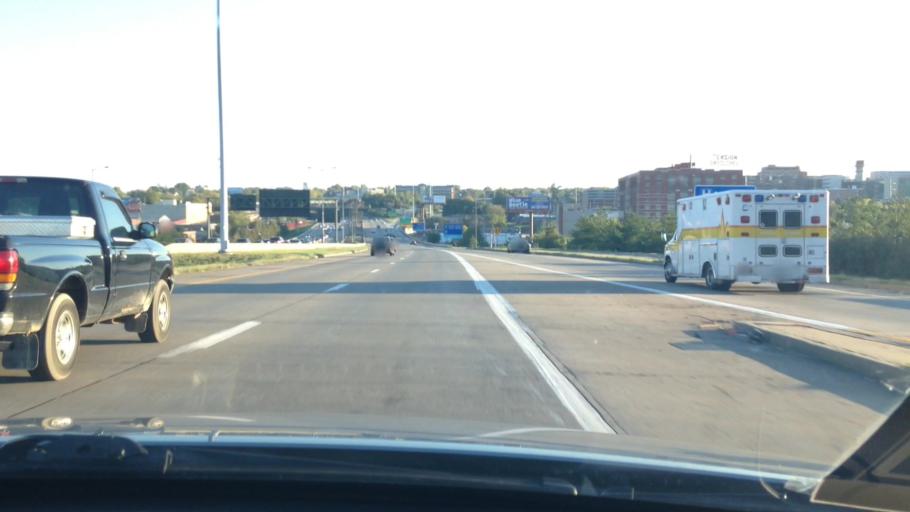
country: US
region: Missouri
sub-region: Jackson County
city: Kansas City
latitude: 39.0943
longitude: -94.5723
